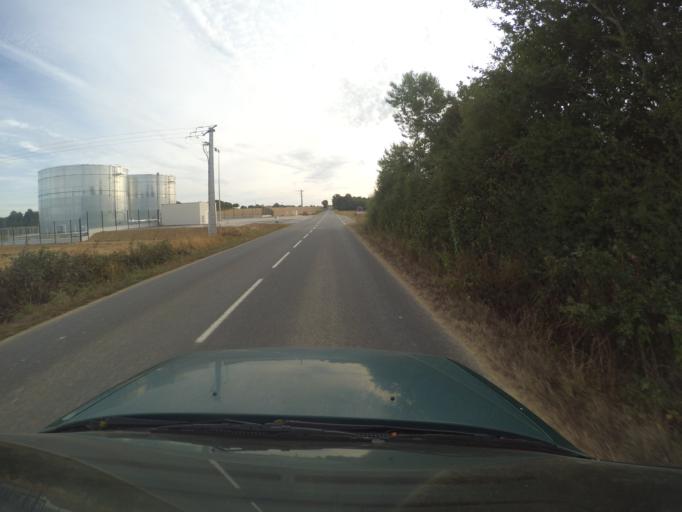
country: FR
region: Pays de la Loire
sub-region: Departement de la Vendee
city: Saint-Andre-Treize-Voies
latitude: 46.9043
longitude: -1.3937
